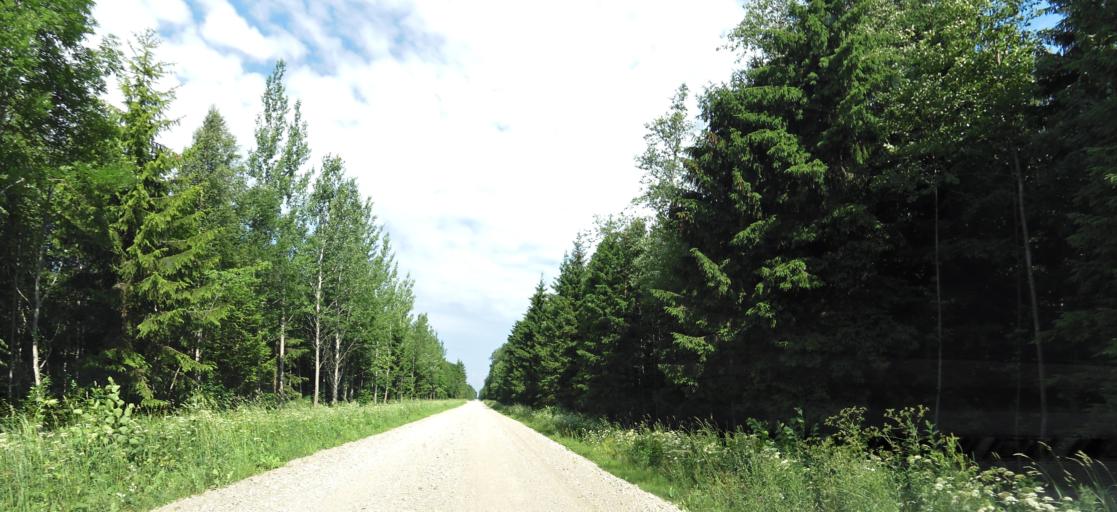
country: LT
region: Panevezys
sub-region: Birzai
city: Birzai
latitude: 56.2331
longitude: 24.9898
